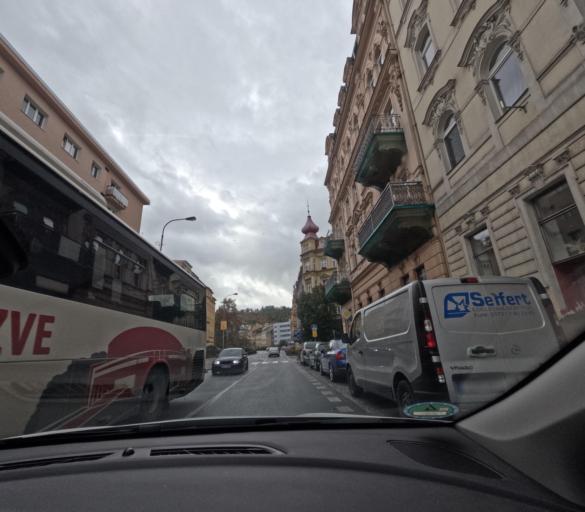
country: CZ
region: Karlovarsky
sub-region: Okres Karlovy Vary
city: Karlovy Vary
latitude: 50.2337
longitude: 12.8730
